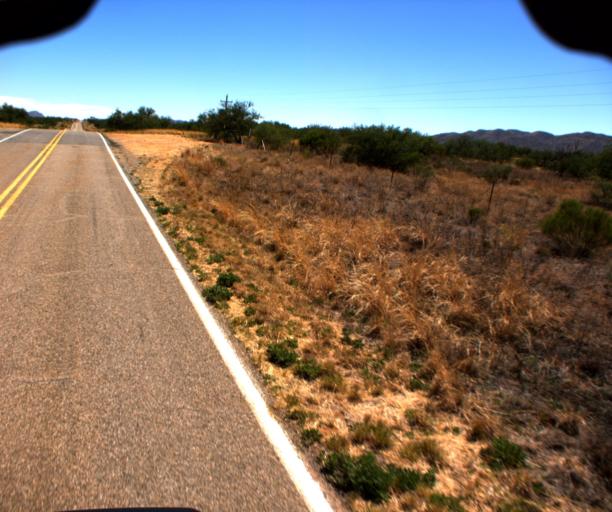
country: US
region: Arizona
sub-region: Pima County
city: Sells
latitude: 31.5748
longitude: -111.5377
